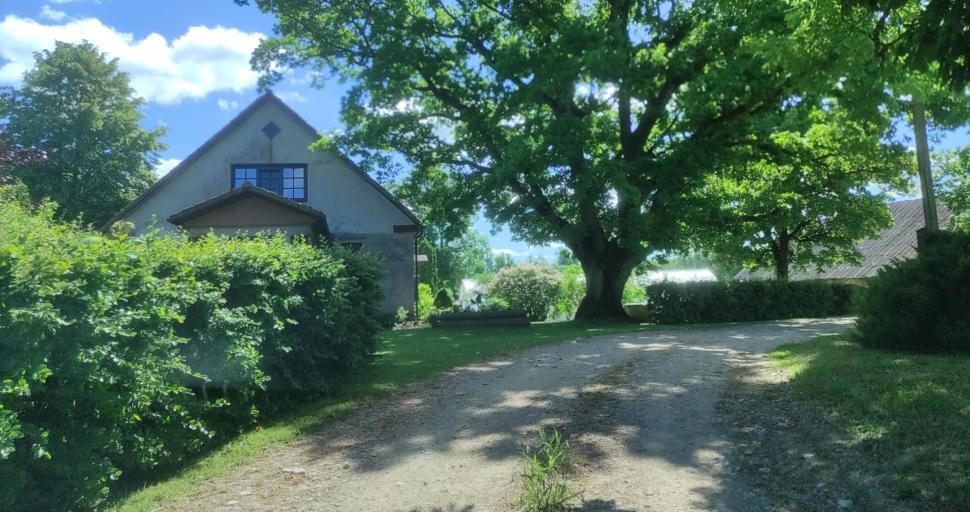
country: LV
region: Aizpute
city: Aizpute
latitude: 56.8698
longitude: 21.7193
